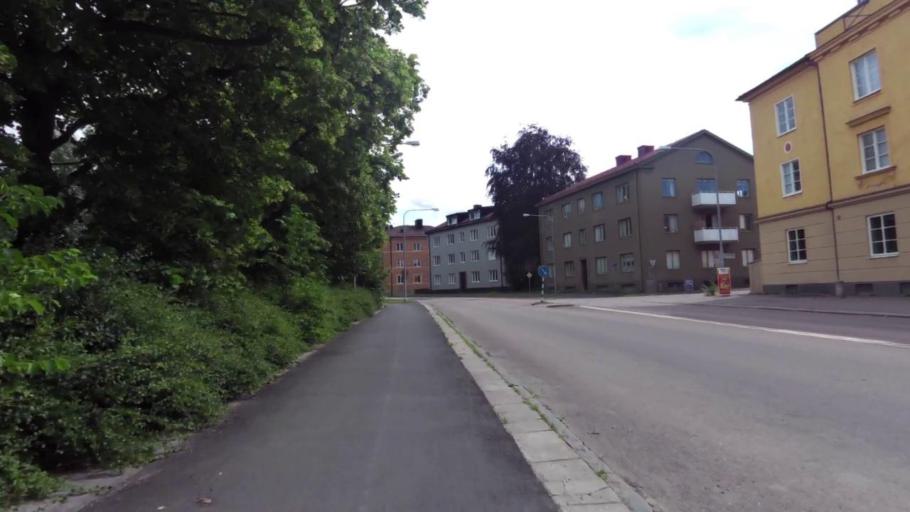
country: SE
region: OEstergoetland
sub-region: Linkopings Kommun
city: Linkoping
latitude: 58.4125
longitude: 15.6066
